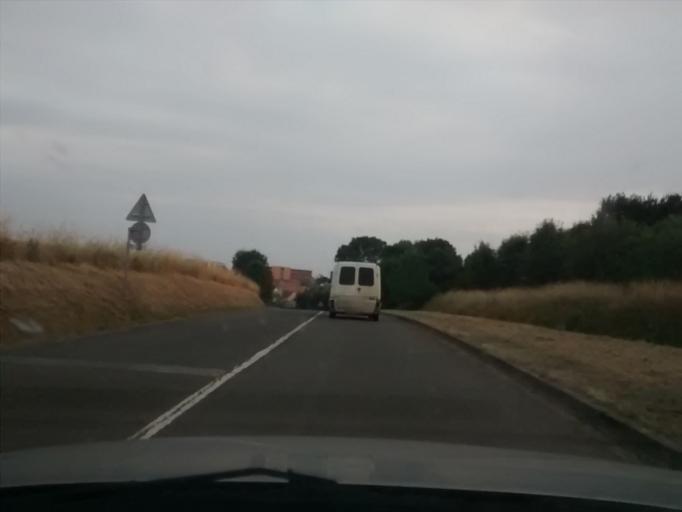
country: FR
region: Pays de la Loire
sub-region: Departement de la Sarthe
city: La Chapelle-Saint-Aubin
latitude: 48.0250
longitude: 0.1602
